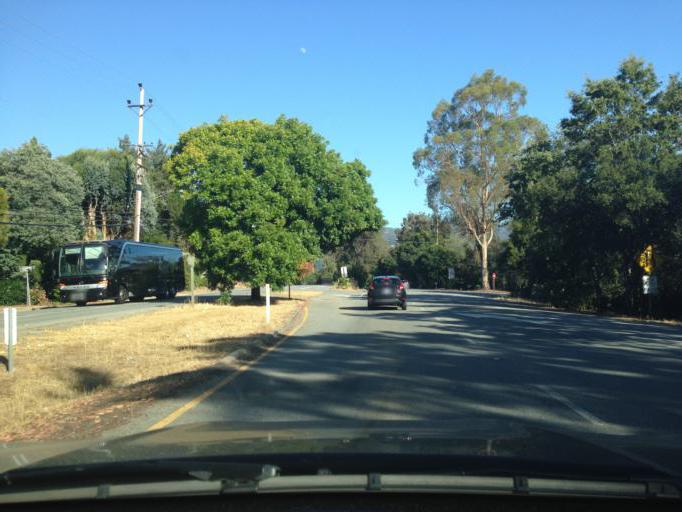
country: US
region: California
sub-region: Santa Clara County
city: Monte Sereno
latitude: 37.2357
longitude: -121.9916
